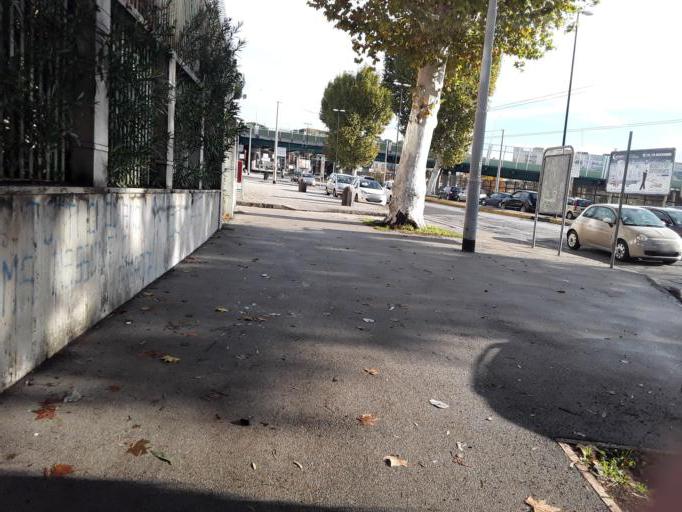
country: IT
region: Campania
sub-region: Provincia di Napoli
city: Napoli
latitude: 40.8681
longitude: 14.2733
